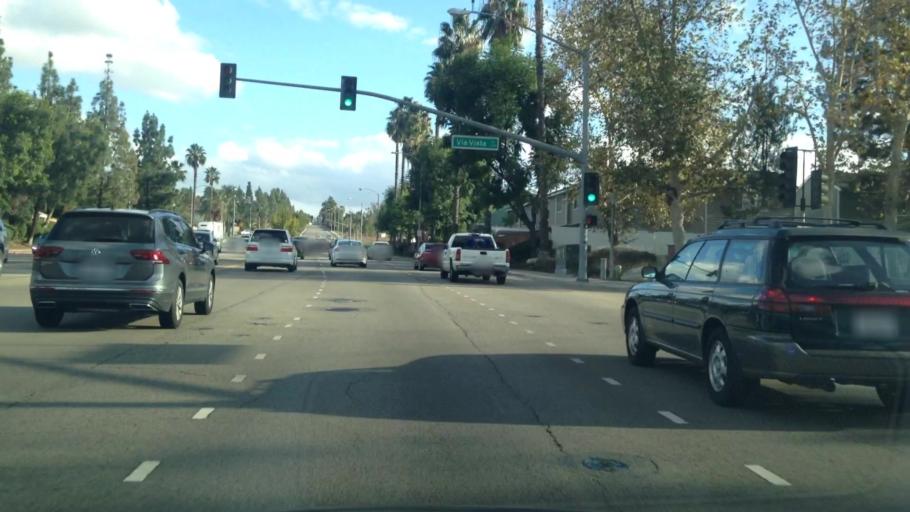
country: US
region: California
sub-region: Riverside County
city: Woodcrest
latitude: 33.9317
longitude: -117.3485
